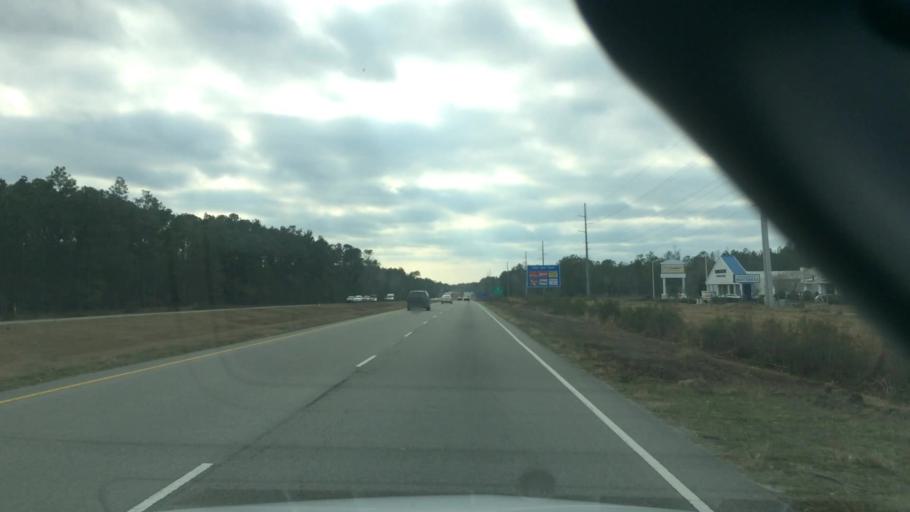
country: US
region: North Carolina
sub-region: Brunswick County
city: Shallotte
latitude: 33.9845
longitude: -78.3944
